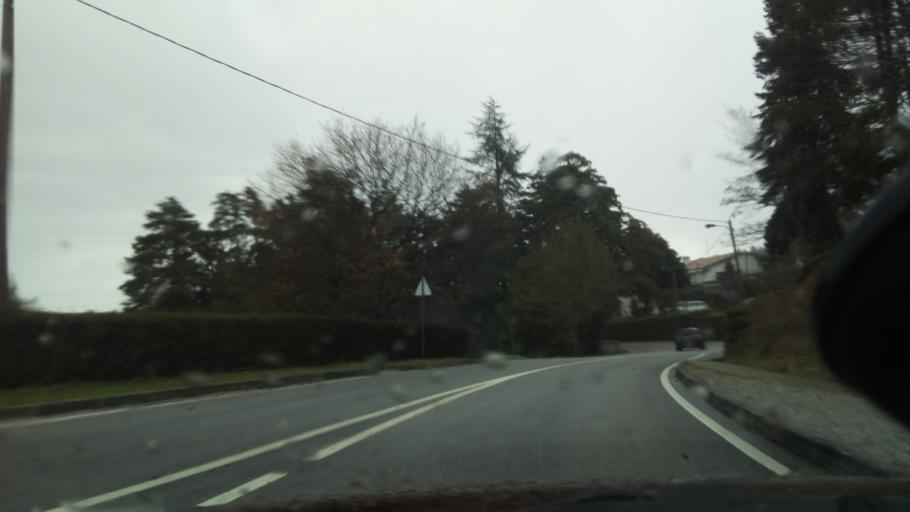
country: PT
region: Guarda
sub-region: Manteigas
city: Manteigas
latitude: 40.4997
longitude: -7.5896
